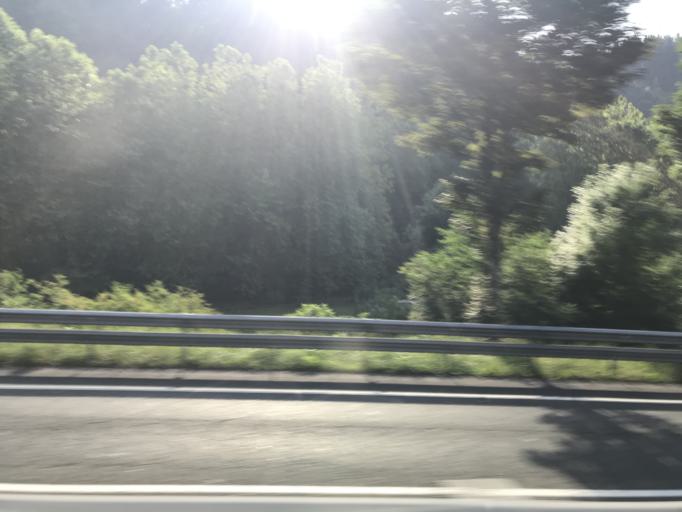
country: ES
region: Basque Country
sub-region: Provincia de Guipuzcoa
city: Arama
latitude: 43.0604
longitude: -2.1709
